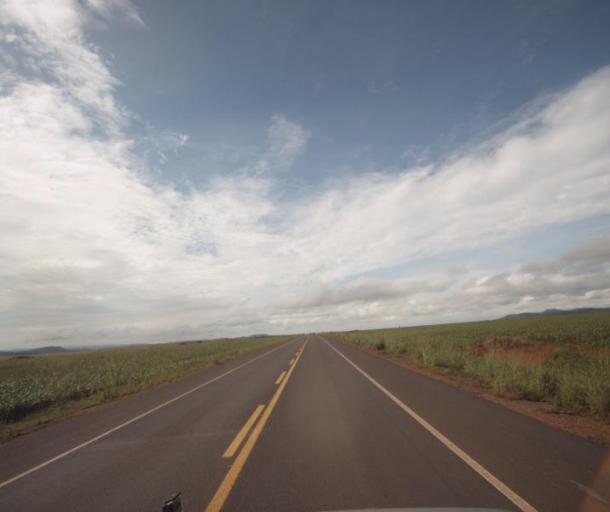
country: BR
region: Goias
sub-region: Padre Bernardo
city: Padre Bernardo
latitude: -15.4036
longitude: -48.6312
